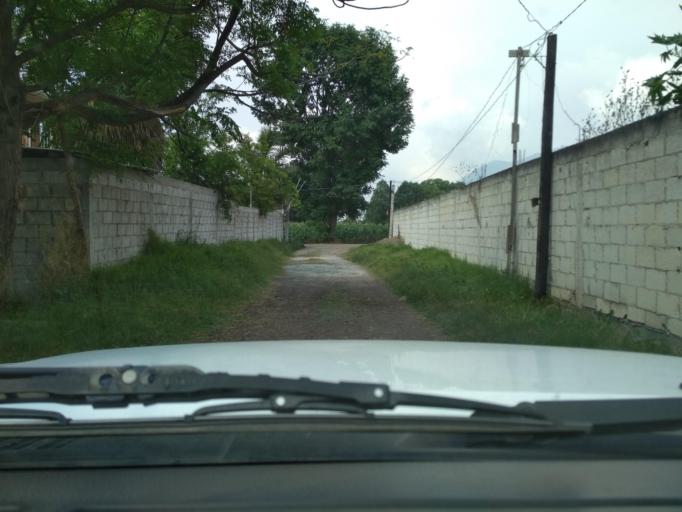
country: MX
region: Veracruz
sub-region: Acultzingo
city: Sierra de Agua
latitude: 18.7559
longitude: -97.2350
